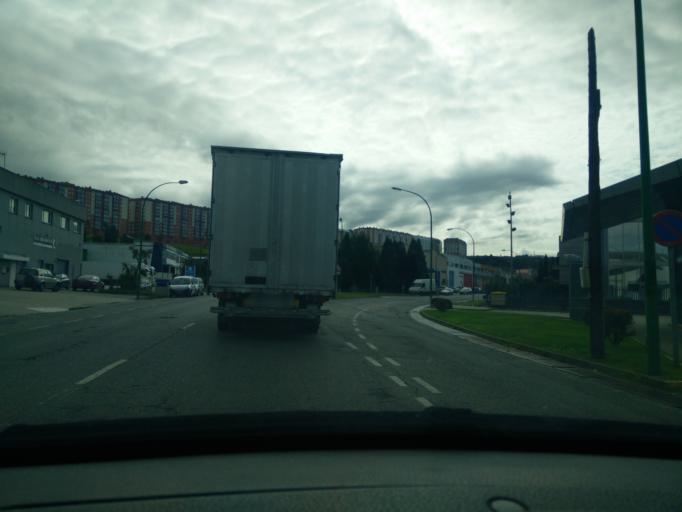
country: ES
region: Galicia
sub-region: Provincia da Coruna
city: A Coruna
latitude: 43.3292
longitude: -8.4322
